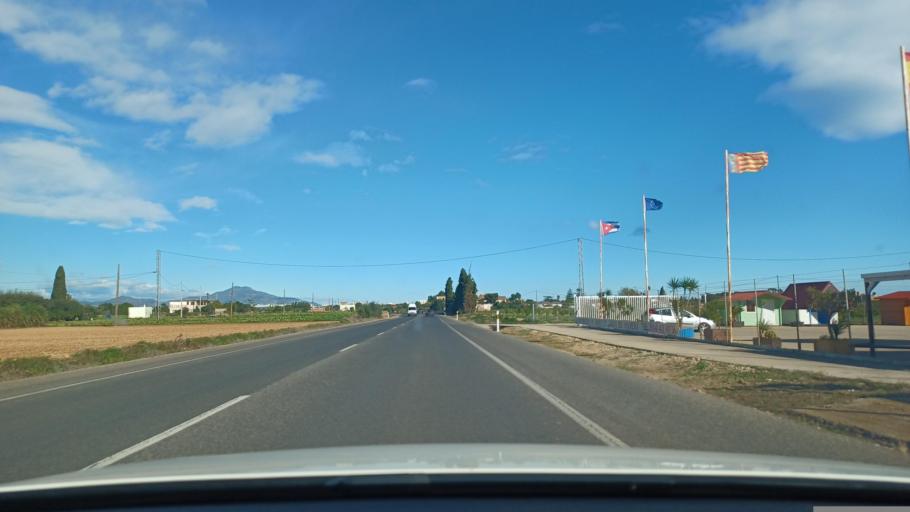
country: ES
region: Valencia
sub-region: Provincia de Castello
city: Benicarlo
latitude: 40.4435
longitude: 0.4456
